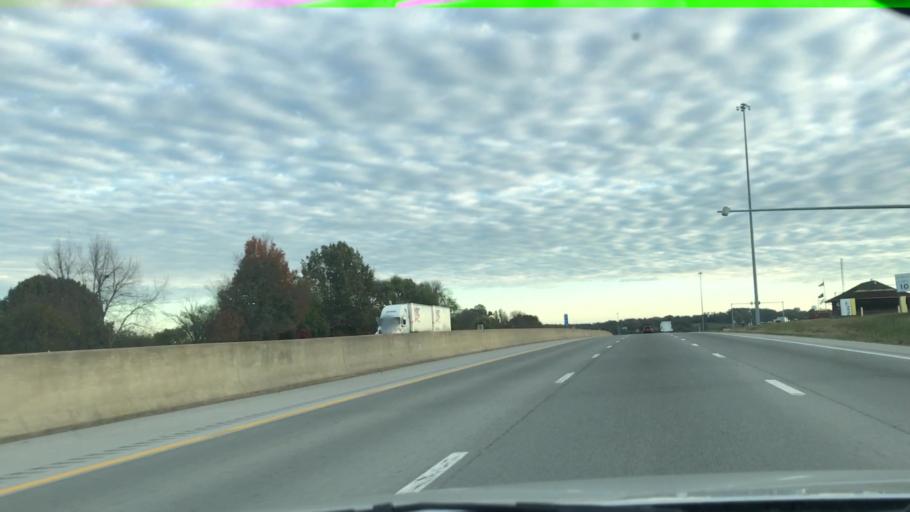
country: US
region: Kentucky
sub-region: Simpson County
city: Franklin
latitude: 36.6858
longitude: -86.5392
